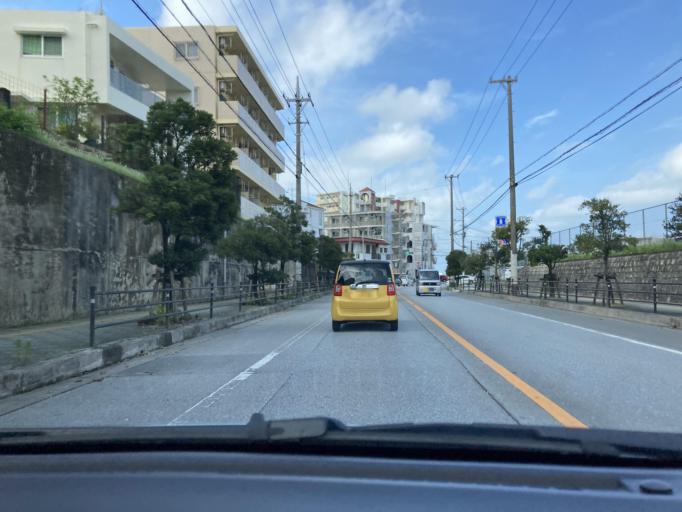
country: JP
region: Okinawa
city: Ginowan
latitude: 26.2615
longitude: 127.7535
